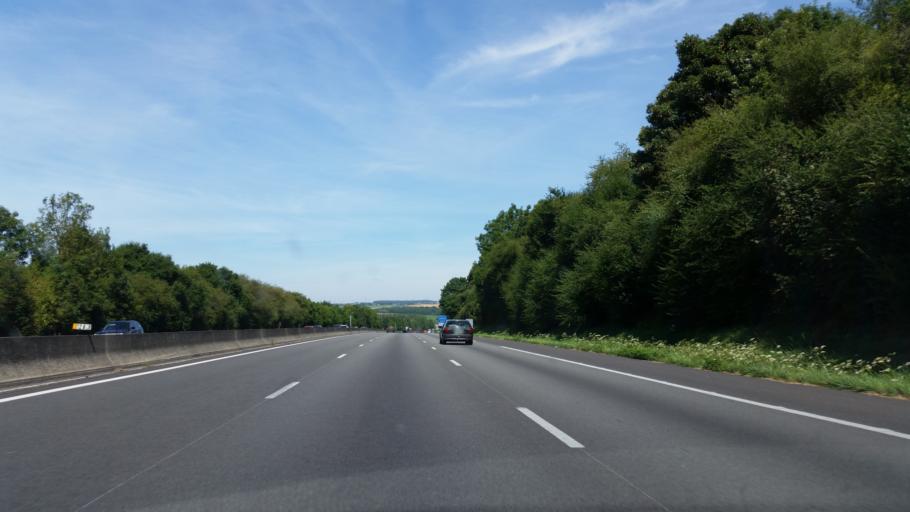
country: FR
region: Picardie
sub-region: Departement de la Somme
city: Peronne
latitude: 49.9368
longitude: 2.8521
